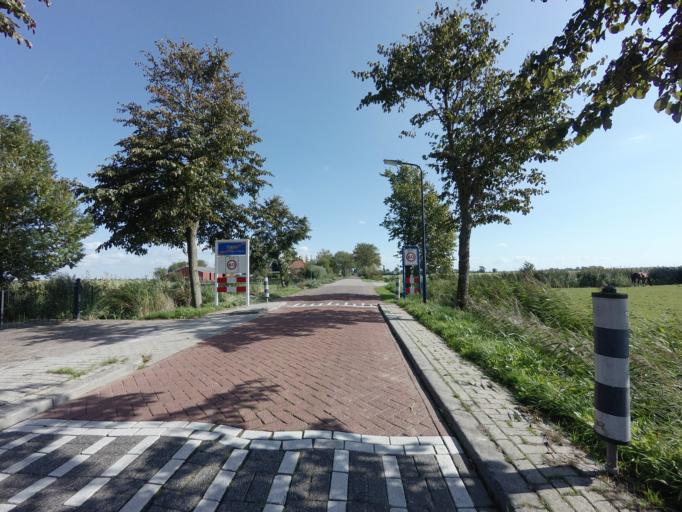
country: NL
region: Friesland
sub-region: Gemeente Littenseradiel
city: Makkum
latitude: 53.0990
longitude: 5.6482
